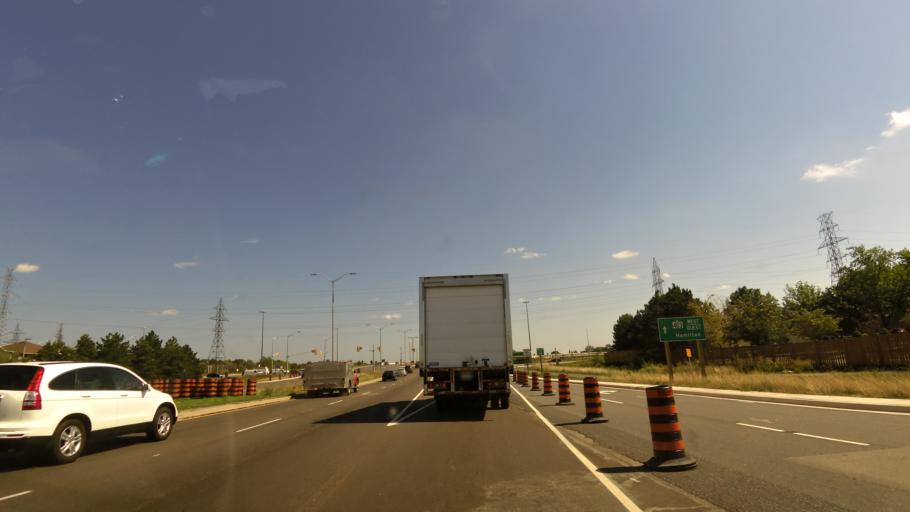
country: CA
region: Ontario
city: Mississauga
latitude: 43.5554
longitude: -79.7003
